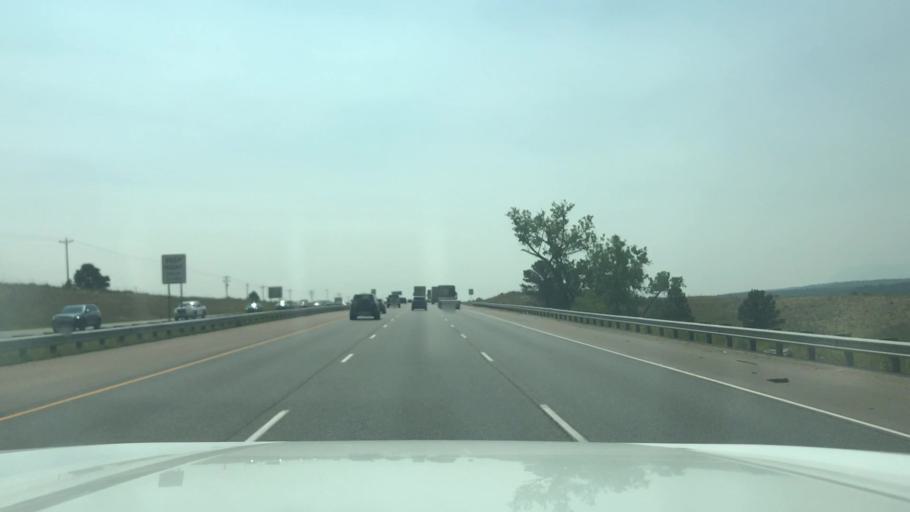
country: US
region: Colorado
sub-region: El Paso County
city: Gleneagle
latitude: 39.0491
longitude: -104.8476
